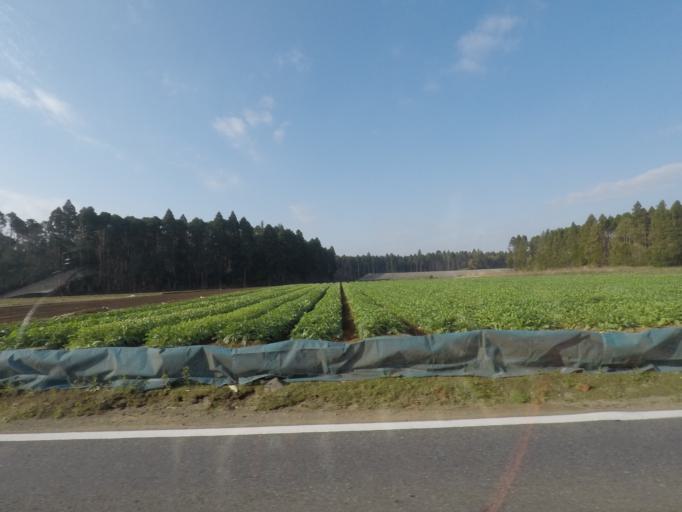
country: JP
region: Chiba
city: Yachimata
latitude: 35.6213
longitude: 140.2500
